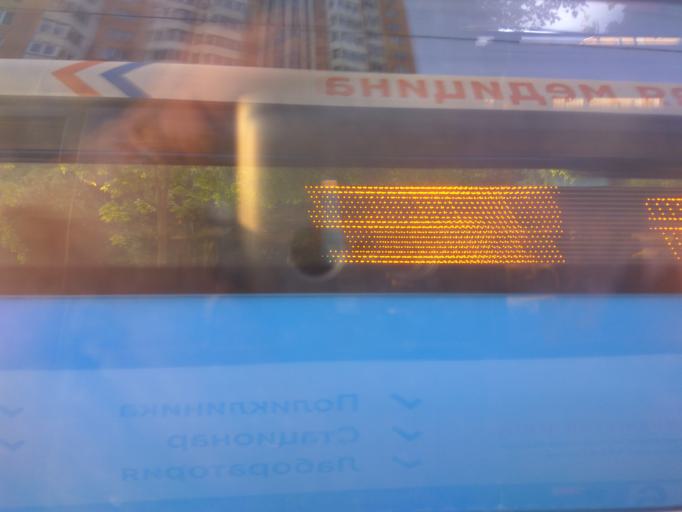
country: RU
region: Moscow
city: Orekhovo-Borisovo Severnoye
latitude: 55.6176
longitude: 37.6994
